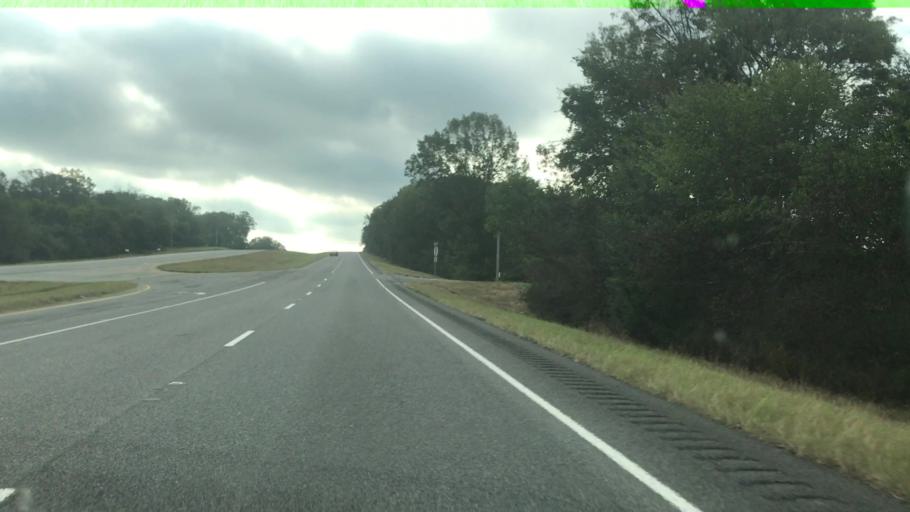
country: US
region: Alabama
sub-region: Morgan County
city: Danville
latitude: 34.3998
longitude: -87.1307
